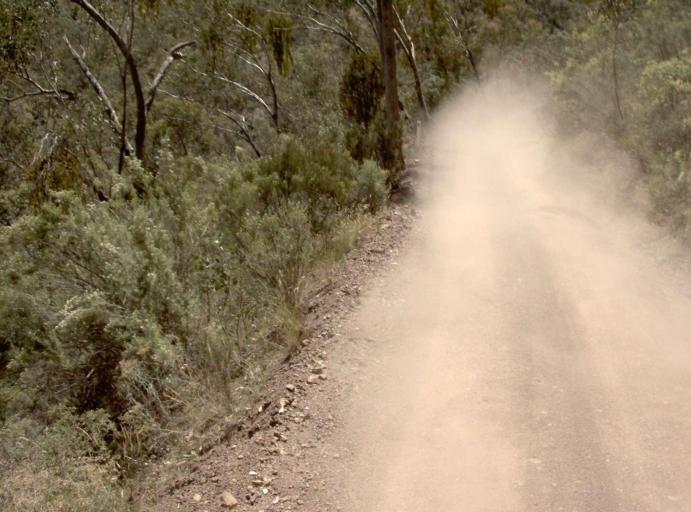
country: AU
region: New South Wales
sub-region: Snowy River
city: Jindabyne
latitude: -37.0855
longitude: 148.3975
